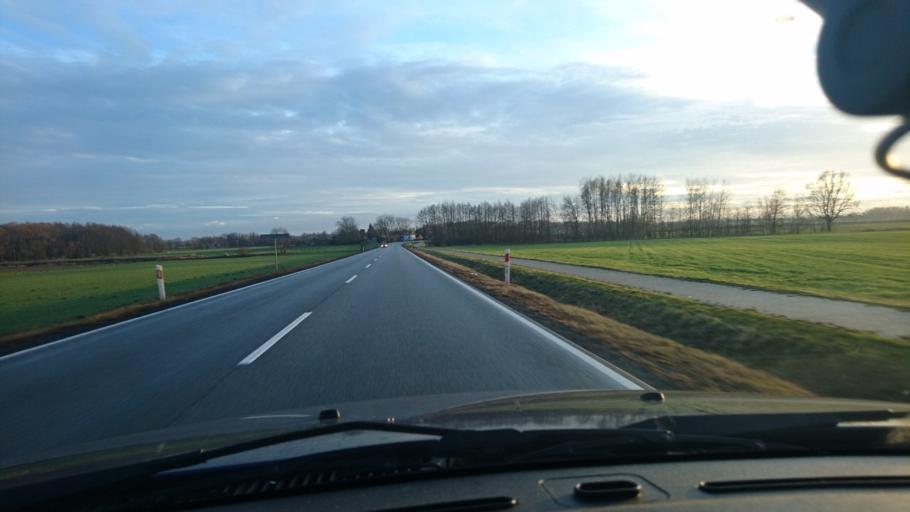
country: PL
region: Greater Poland Voivodeship
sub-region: Powiat kepinski
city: Opatow
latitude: 51.1730
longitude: 18.1454
